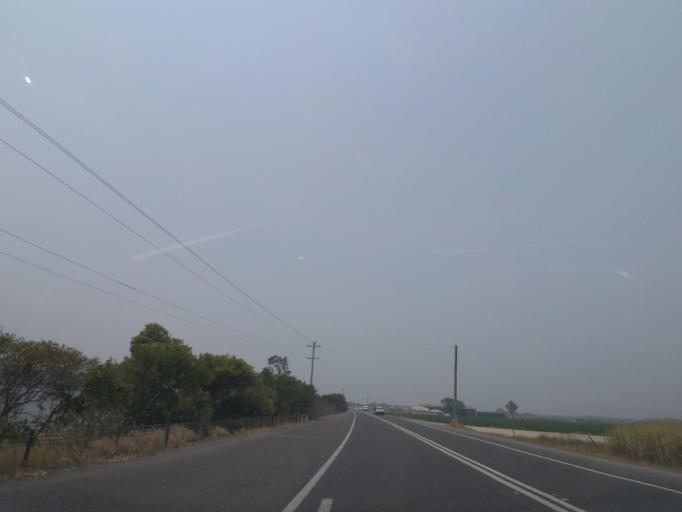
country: AU
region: New South Wales
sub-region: Richmond Valley
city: Evans Head
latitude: -28.9958
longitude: 153.4550
